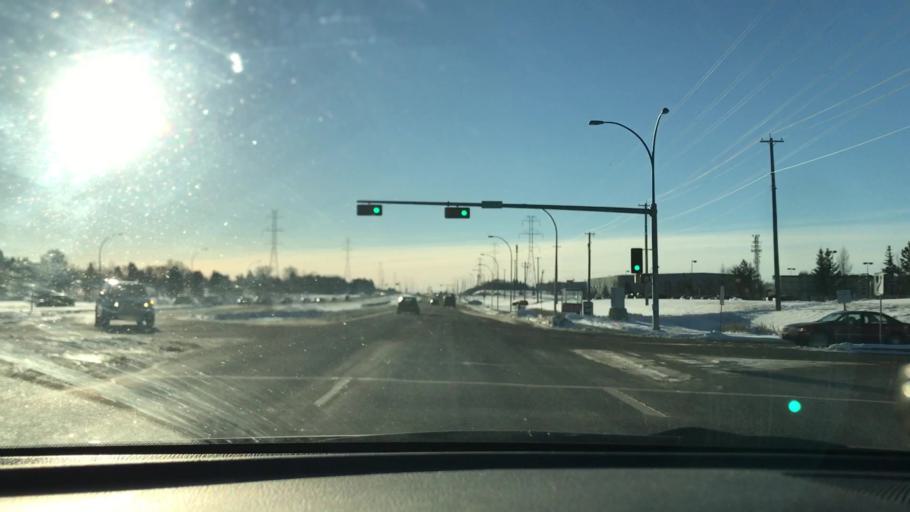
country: CA
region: Alberta
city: Edmonton
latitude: 53.4569
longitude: -113.4669
